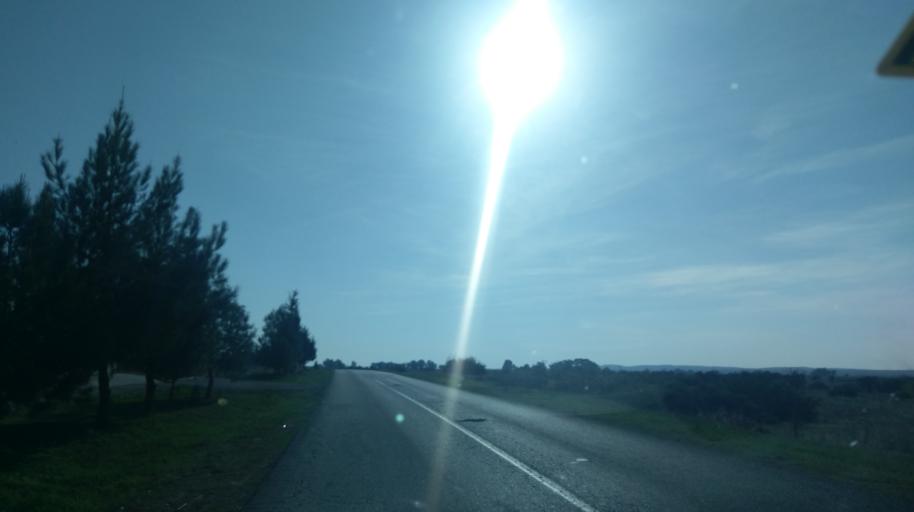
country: CY
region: Larnaka
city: Pergamos
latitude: 35.0878
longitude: 33.7224
